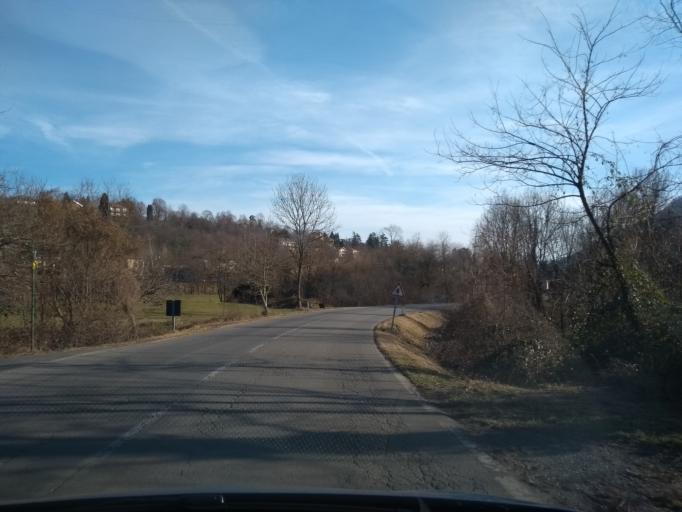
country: IT
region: Piedmont
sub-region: Provincia di Torino
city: Lanzo Torinese
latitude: 45.2812
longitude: 7.4762
